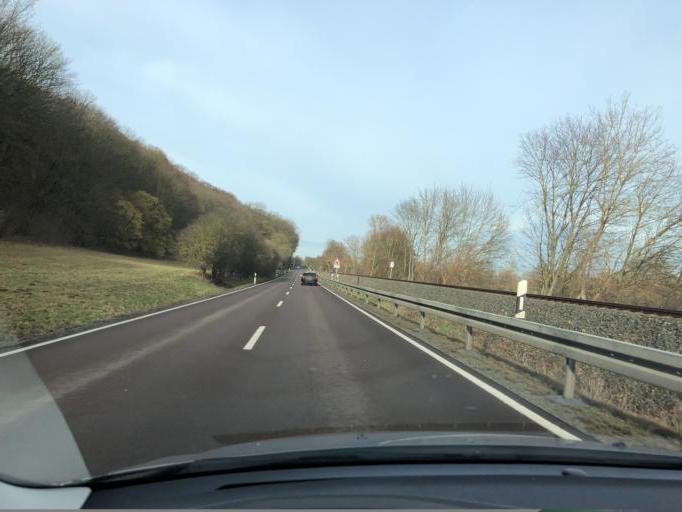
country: DE
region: Saxony-Anhalt
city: Balgstadt
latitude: 51.2118
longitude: 11.7149
